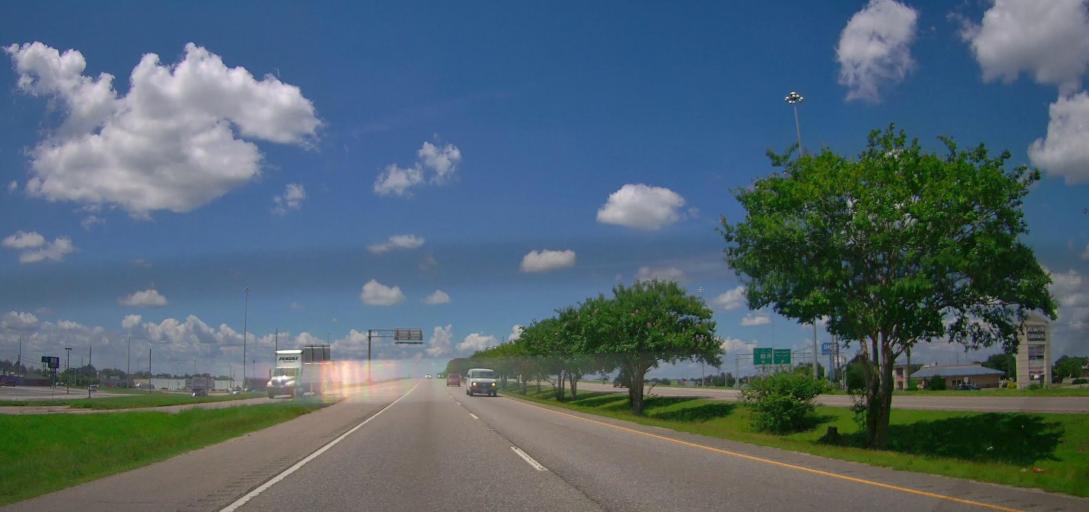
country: US
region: Alabama
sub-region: Montgomery County
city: Montgomery
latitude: 32.3792
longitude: -86.2099
